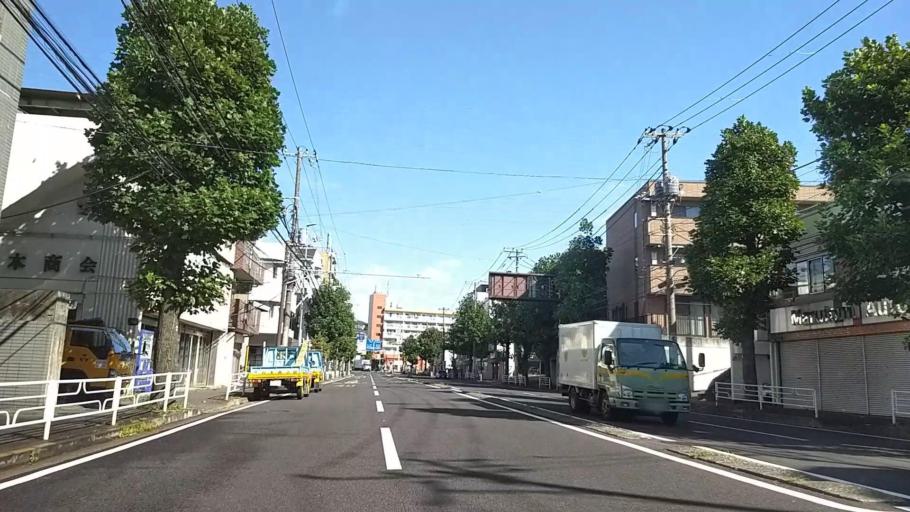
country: JP
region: Kanagawa
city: Yokohama
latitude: 35.4930
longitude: 139.6202
